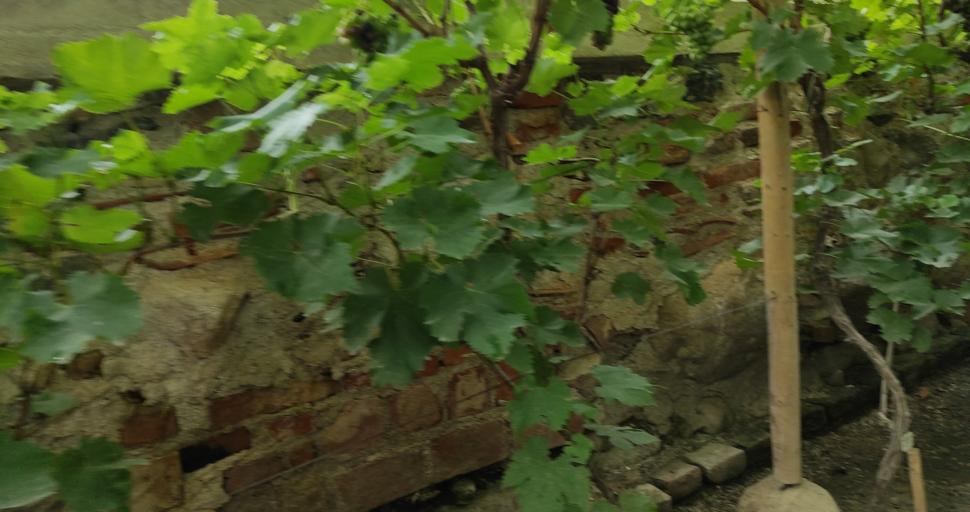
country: LV
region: Talsu Rajons
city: Talsi
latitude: 57.2270
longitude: 22.7626
